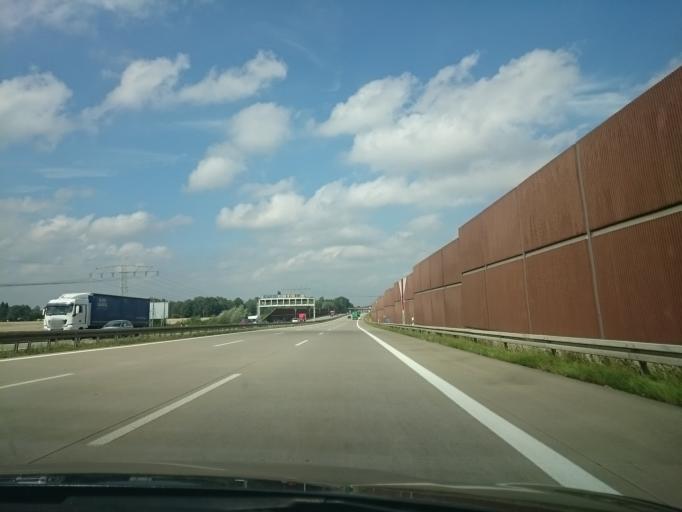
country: DE
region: Brandenburg
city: Neuenhagen
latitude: 52.5095
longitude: 13.7346
